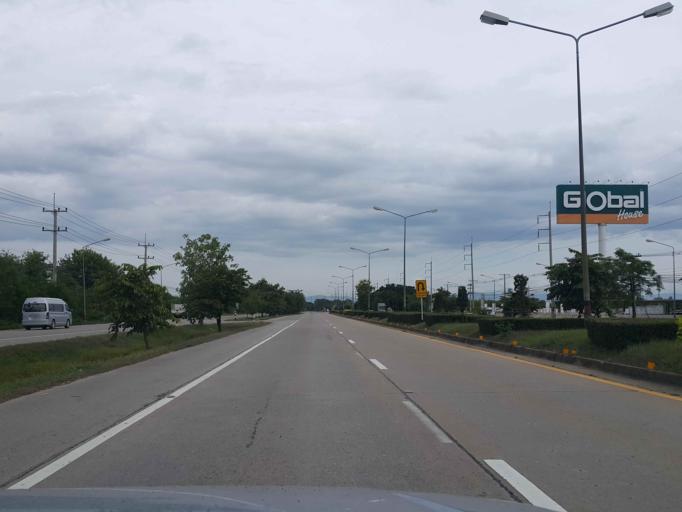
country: TH
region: Lampang
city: Lampang
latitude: 18.2822
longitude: 99.4507
